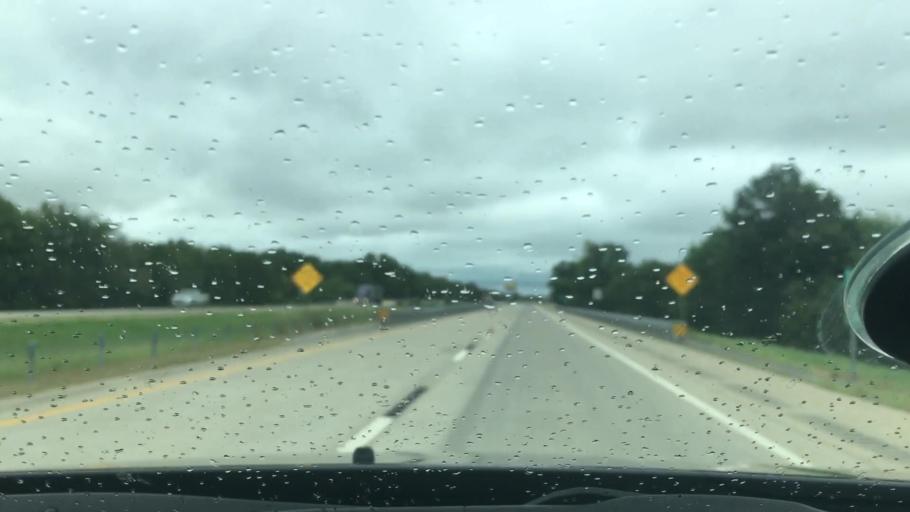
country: US
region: Oklahoma
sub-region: Muskogee County
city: Warner
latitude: 35.4860
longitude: -95.1914
